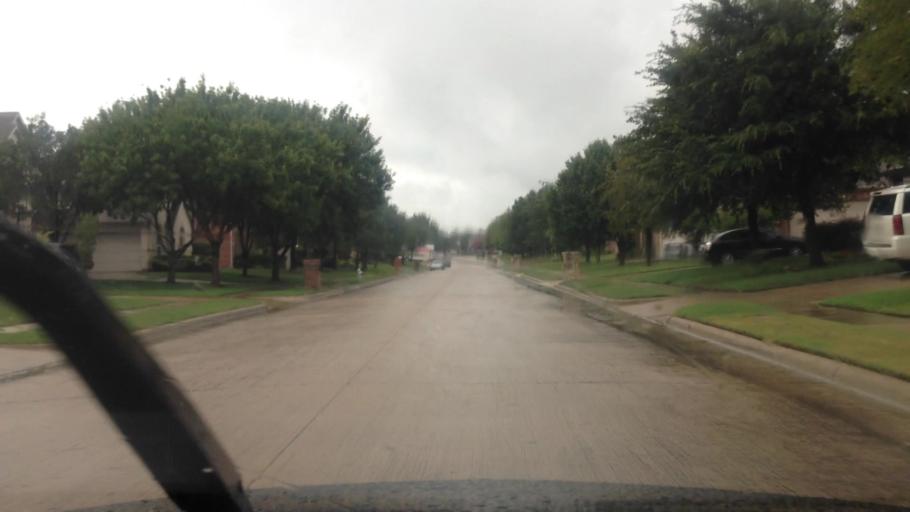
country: US
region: Texas
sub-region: Tarrant County
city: Keller
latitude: 32.9085
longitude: -97.2113
